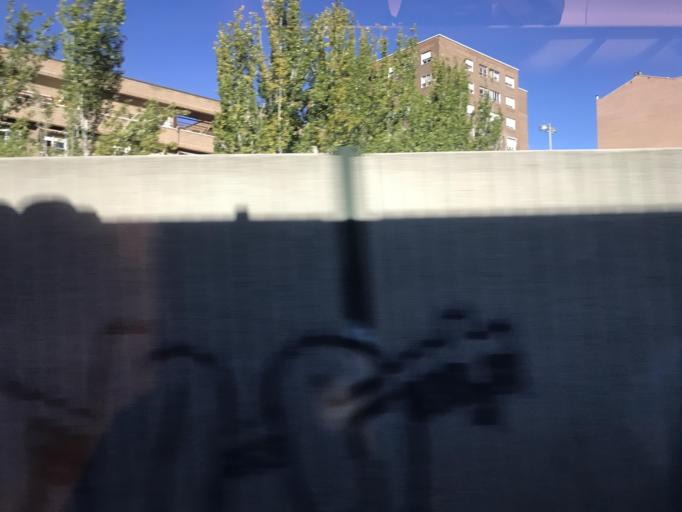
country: ES
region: Castille and Leon
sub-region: Provincia de Valladolid
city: Valladolid
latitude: 41.6394
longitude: -4.7326
